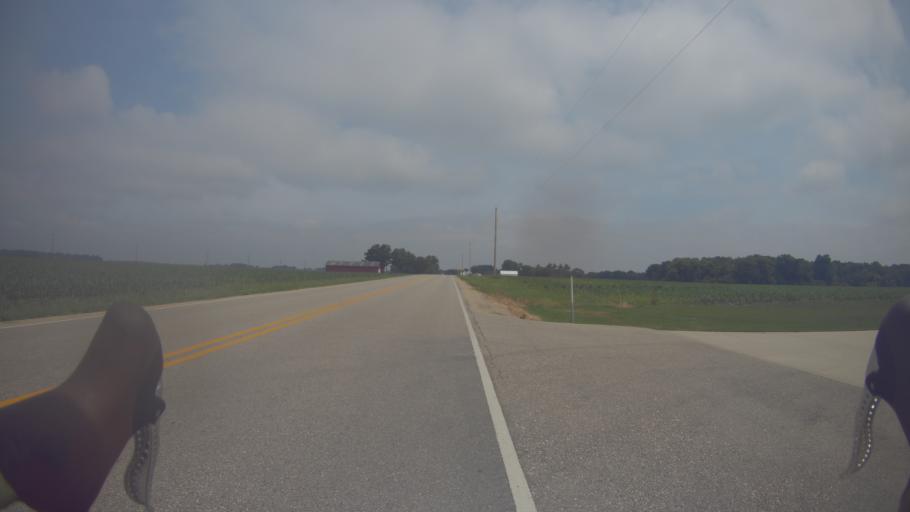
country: US
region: Wisconsin
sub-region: Rock County
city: Edgerton
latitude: 42.8795
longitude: -89.0389
